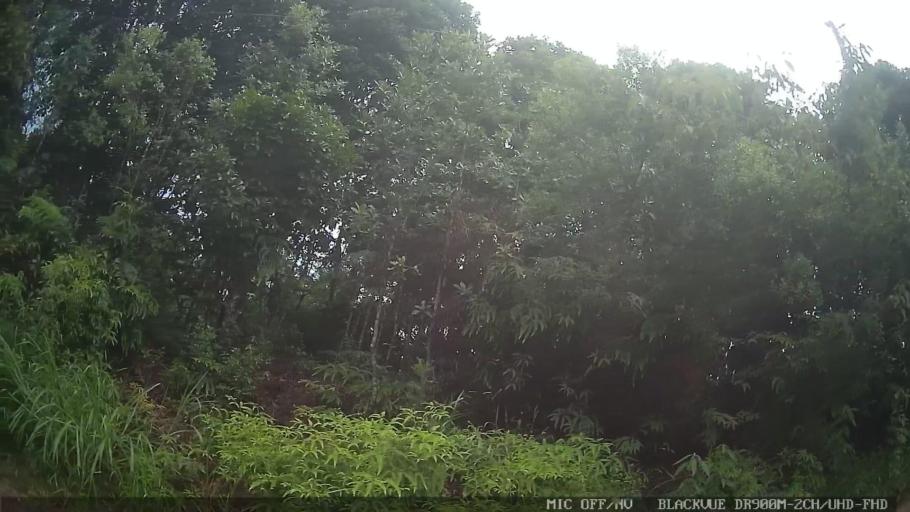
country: BR
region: Sao Paulo
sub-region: Rio Grande Da Serra
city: Rio Grande da Serra
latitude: -23.6909
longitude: -46.3232
